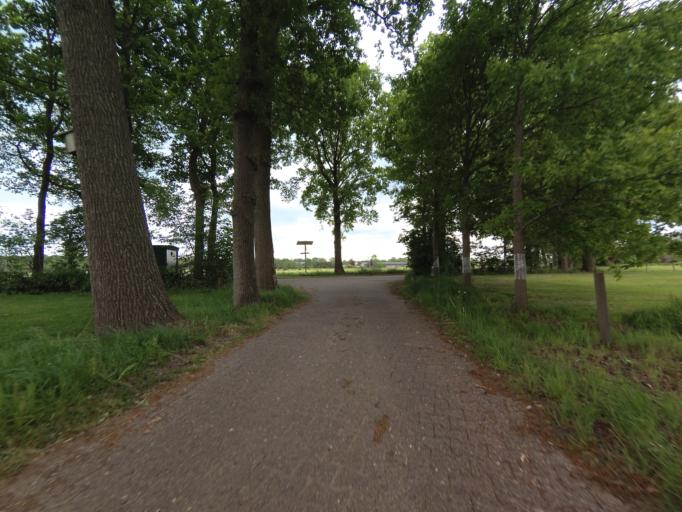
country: NL
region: Utrecht
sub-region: Gemeente Leusden
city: Leusden
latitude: 52.1564
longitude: 5.4398
